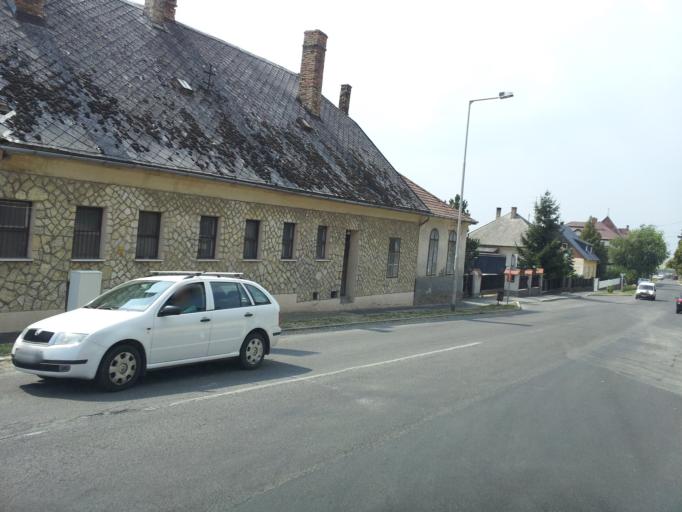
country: HU
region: Gyor-Moson-Sopron
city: Pannonhalma
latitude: 47.5503
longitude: 17.7542
